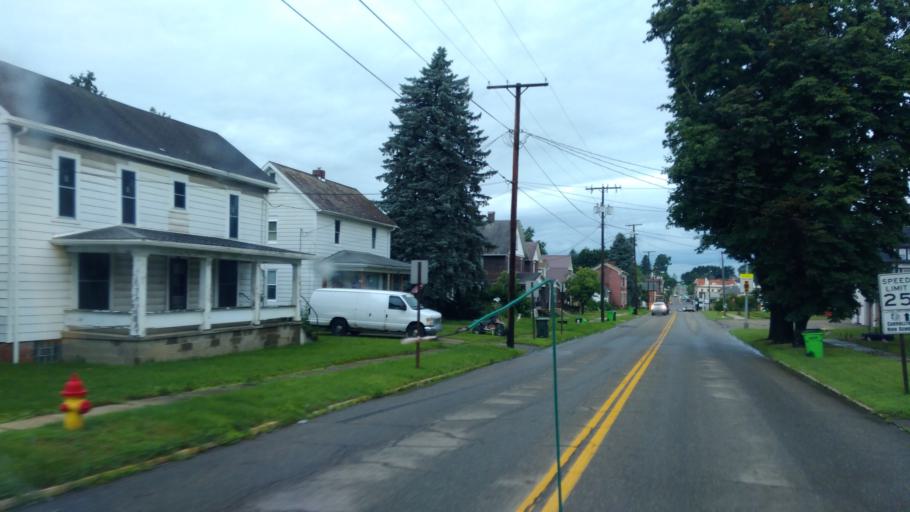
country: US
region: Ohio
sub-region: Carroll County
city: Carrollton
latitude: 40.5709
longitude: -81.0824
